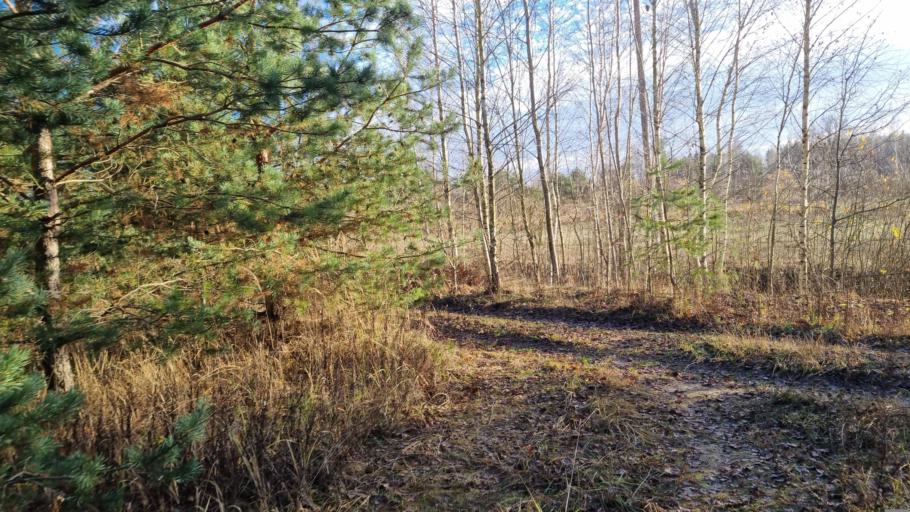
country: LV
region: Kekava
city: Kekava
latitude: 56.8134
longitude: 24.1994
